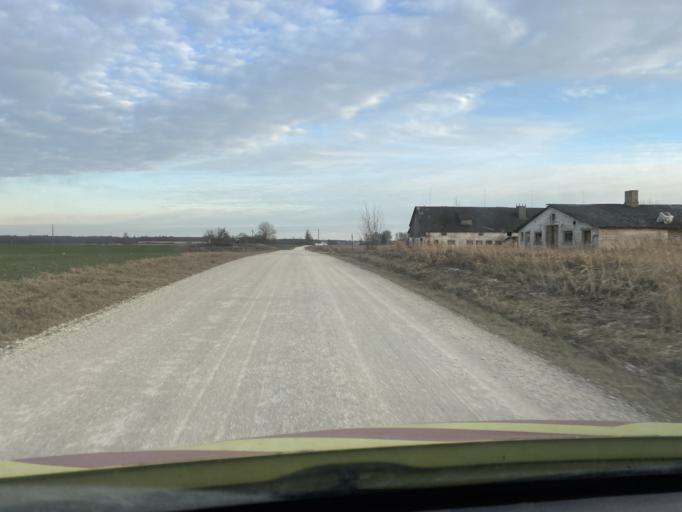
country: EE
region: Jogevamaa
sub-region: Poltsamaa linn
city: Poltsamaa
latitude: 58.5792
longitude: 26.1215
